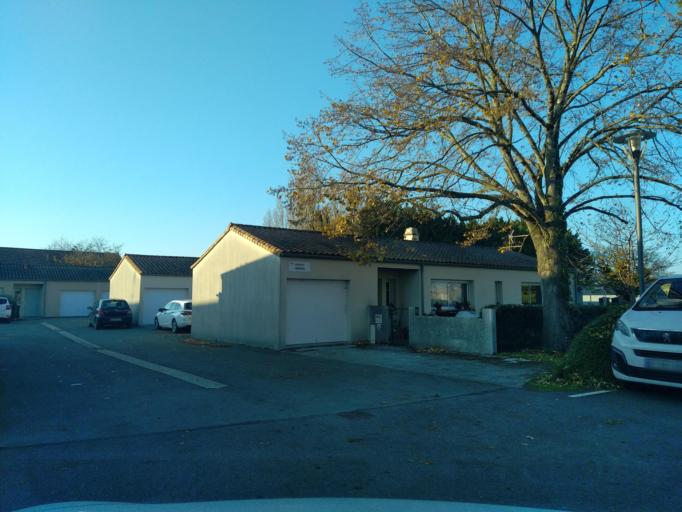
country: FR
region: Pays de la Loire
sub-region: Departement de la Vendee
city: Maillezais
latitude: 46.3425
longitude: -0.7877
